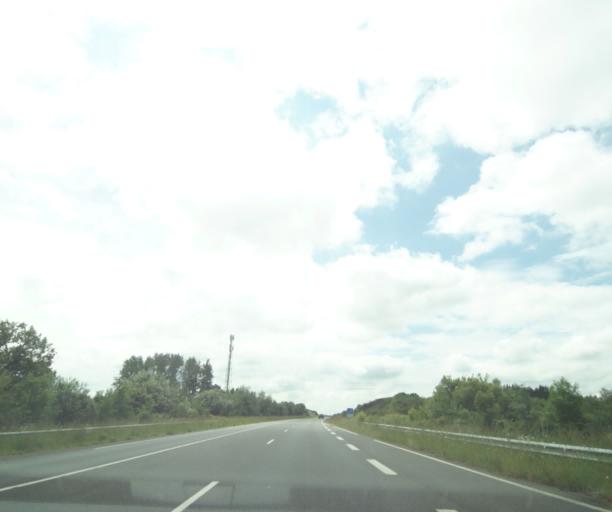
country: FR
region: Poitou-Charentes
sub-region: Departement des Deux-Sevres
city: Saint-Pardoux
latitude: 46.5426
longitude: -0.3130
